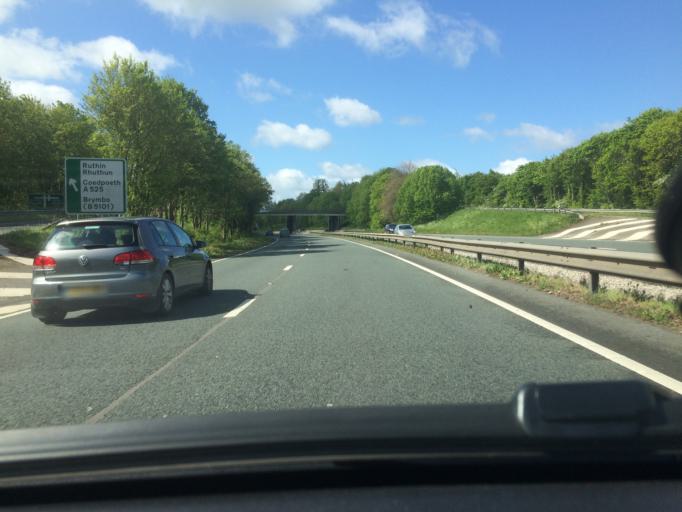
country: GB
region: Wales
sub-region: Wrexham
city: Wrexham
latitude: 53.0473
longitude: -3.0255
